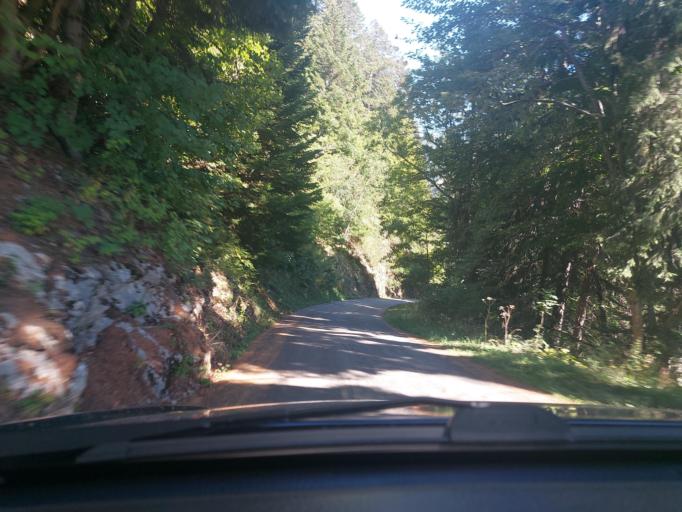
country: CH
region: Vaud
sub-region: Aigle District
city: Aigle
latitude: 46.3586
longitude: 6.9607
